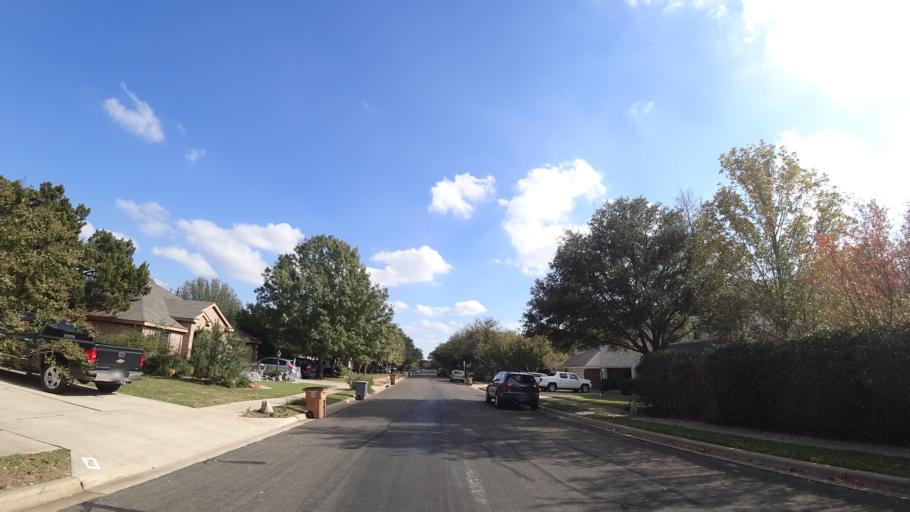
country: US
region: Texas
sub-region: Travis County
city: Shady Hollow
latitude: 30.1828
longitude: -97.8550
